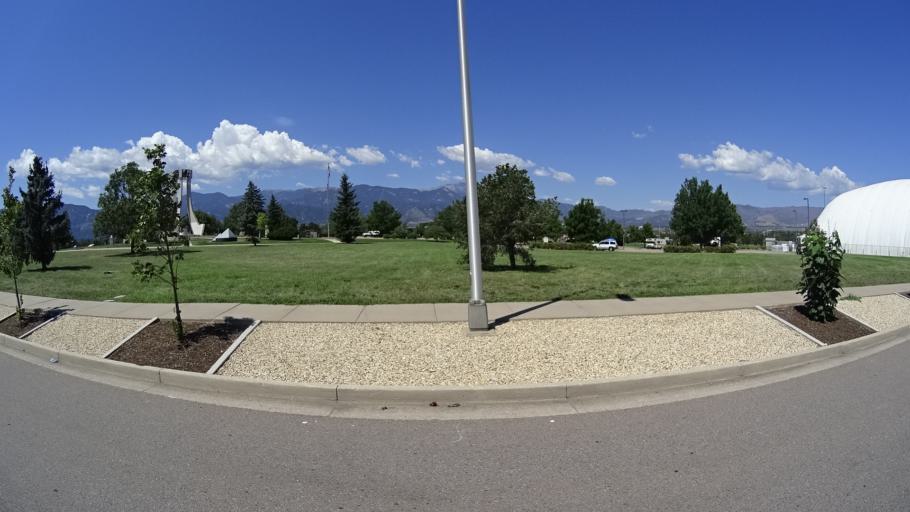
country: US
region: Colorado
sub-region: El Paso County
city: Colorado Springs
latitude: 38.8277
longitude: -104.7951
